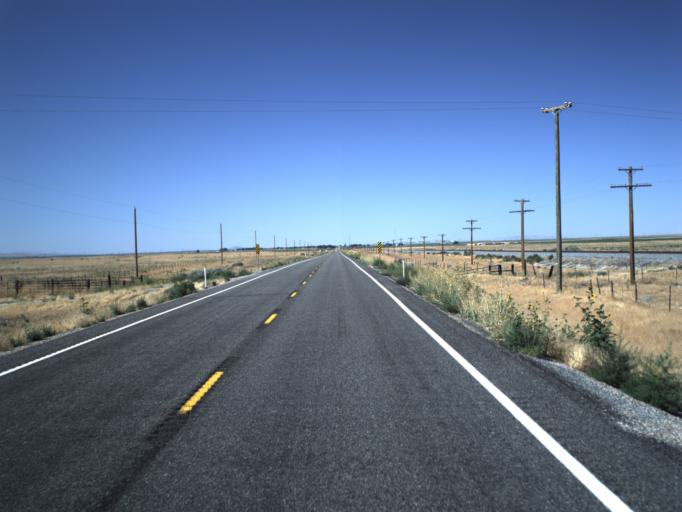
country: US
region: Utah
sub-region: Millard County
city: Delta
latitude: 39.5830
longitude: -112.3353
